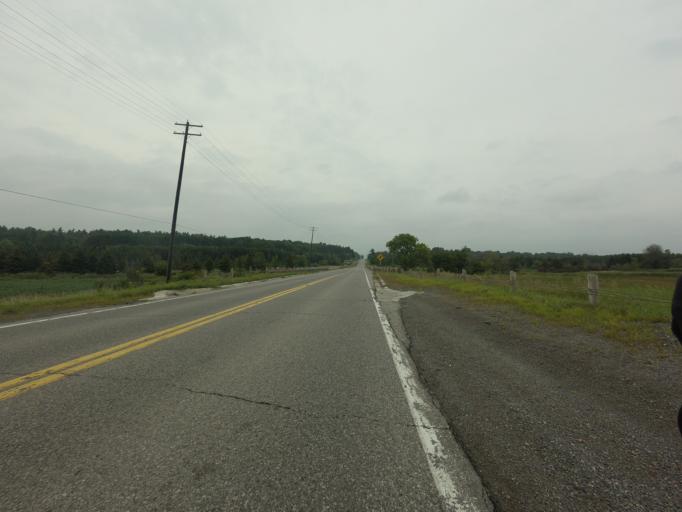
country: CA
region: Ontario
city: Bells Corners
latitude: 45.3396
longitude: -76.0154
